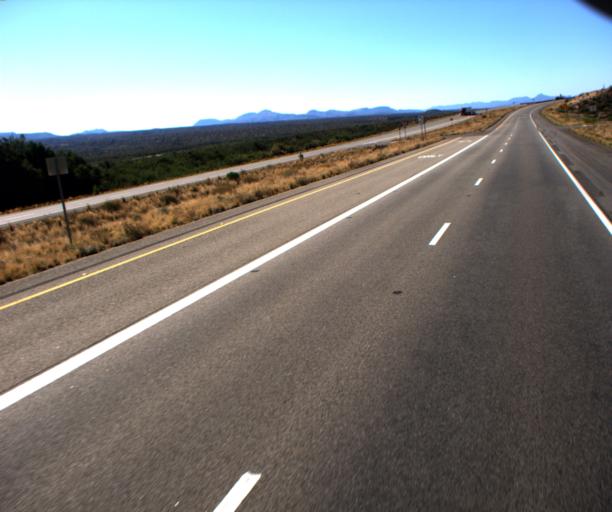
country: US
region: Arizona
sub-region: Yavapai County
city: Bagdad
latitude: 34.8244
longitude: -113.6281
